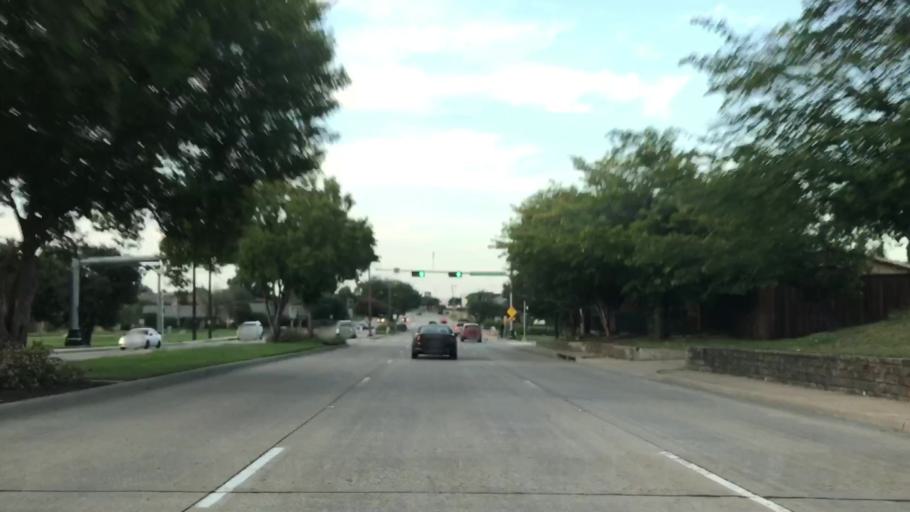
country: US
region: Texas
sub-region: Dallas County
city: Carrollton
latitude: 32.9945
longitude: -96.8890
